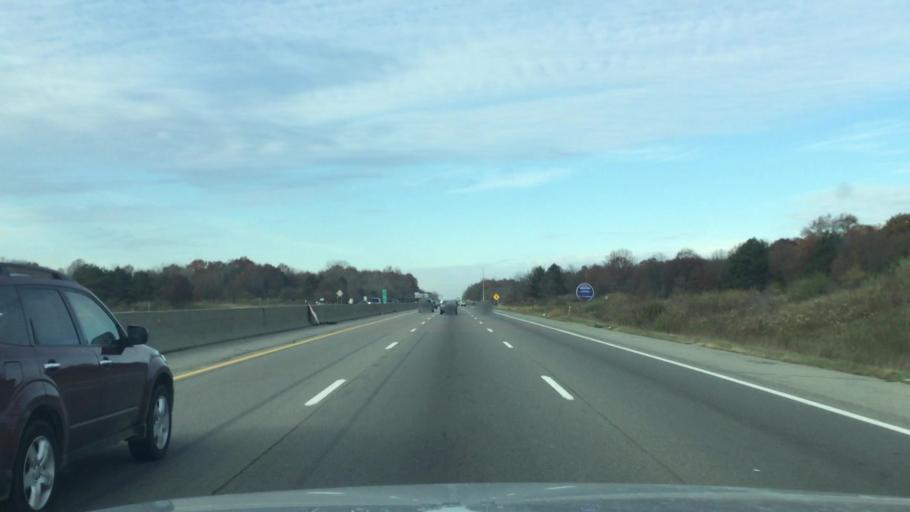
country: US
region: Michigan
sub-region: Washtenaw County
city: Ypsilanti
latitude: 42.2244
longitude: -83.6528
